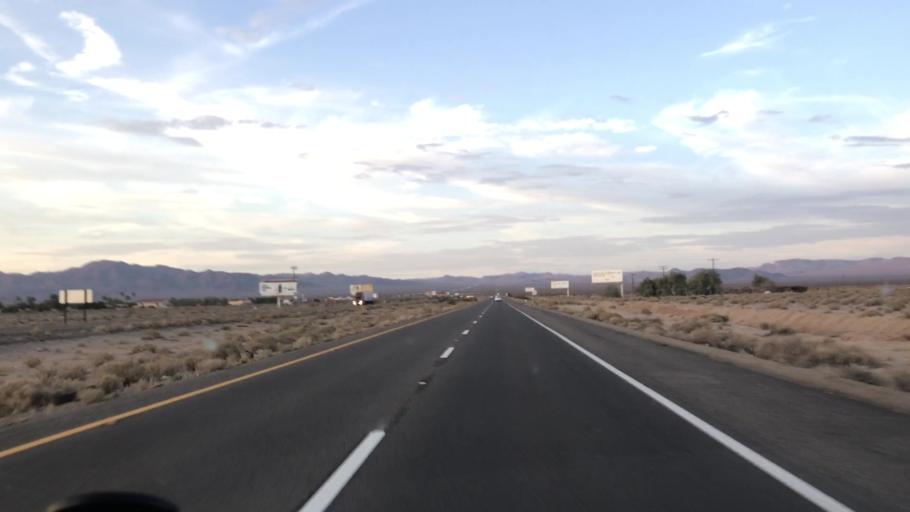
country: US
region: California
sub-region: San Bernardino County
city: Fort Irwin
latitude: 35.2672
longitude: -116.0670
